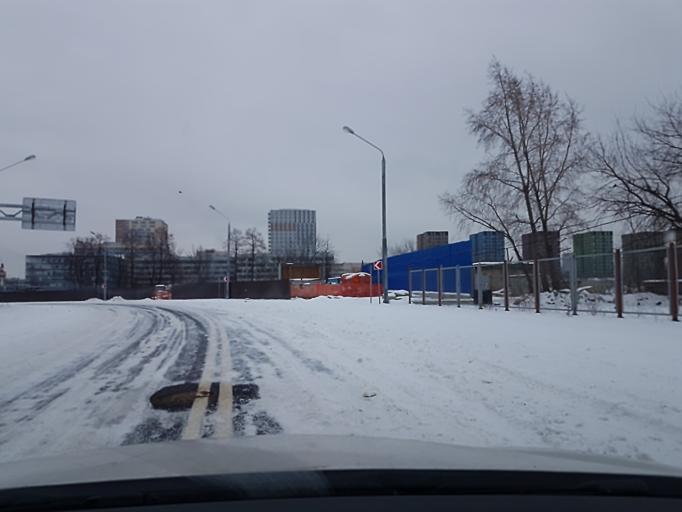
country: RU
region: Moskovskaya
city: Kozhukhovo
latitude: 55.6950
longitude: 37.6552
